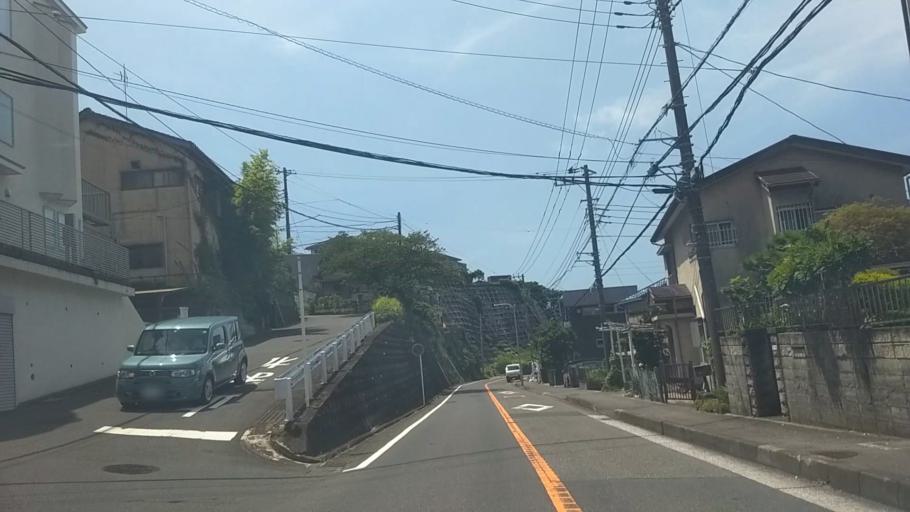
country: JP
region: Kanagawa
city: Kamakura
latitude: 35.3038
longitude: 139.5616
